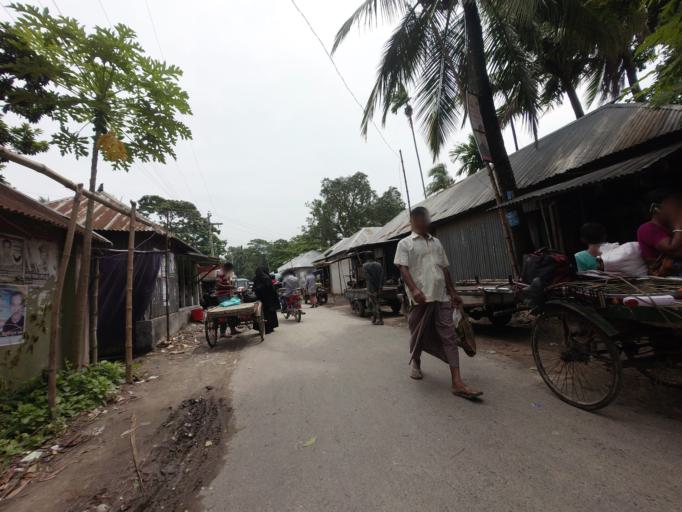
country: BD
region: Khulna
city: Kalia
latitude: 23.0855
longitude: 89.6711
